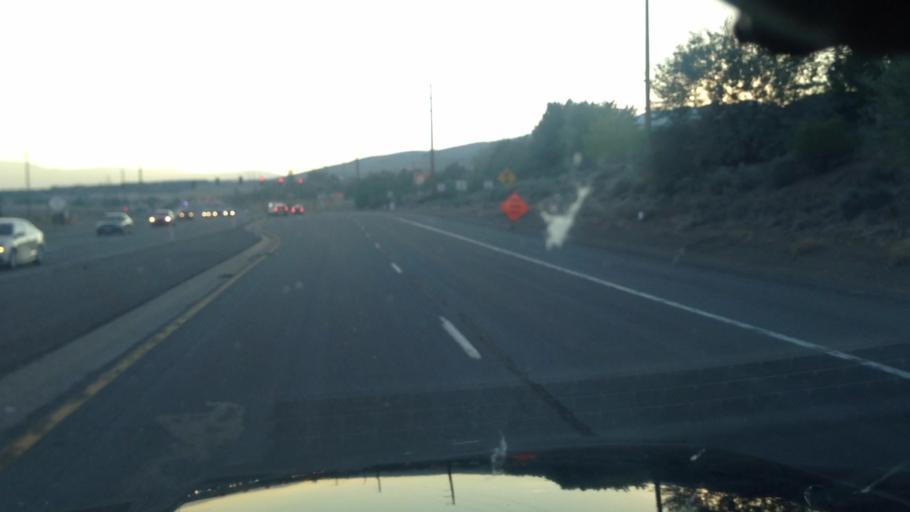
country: US
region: Nevada
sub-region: Washoe County
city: Reno
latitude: 39.5524
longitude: -119.8100
